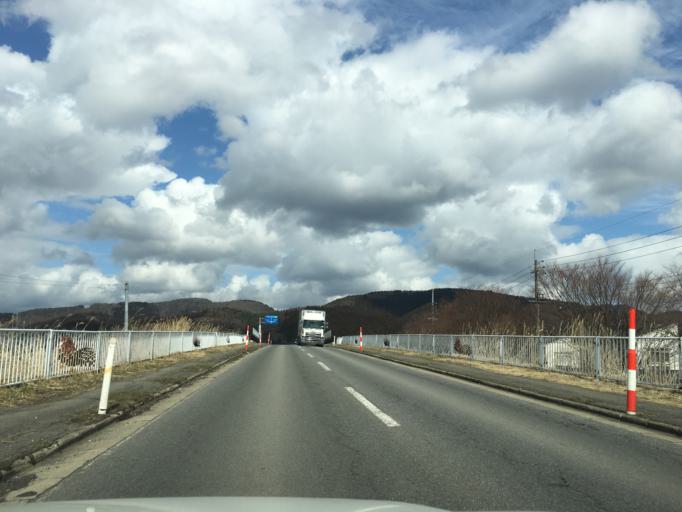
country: JP
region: Akita
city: Odate
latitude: 40.2226
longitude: 140.5886
